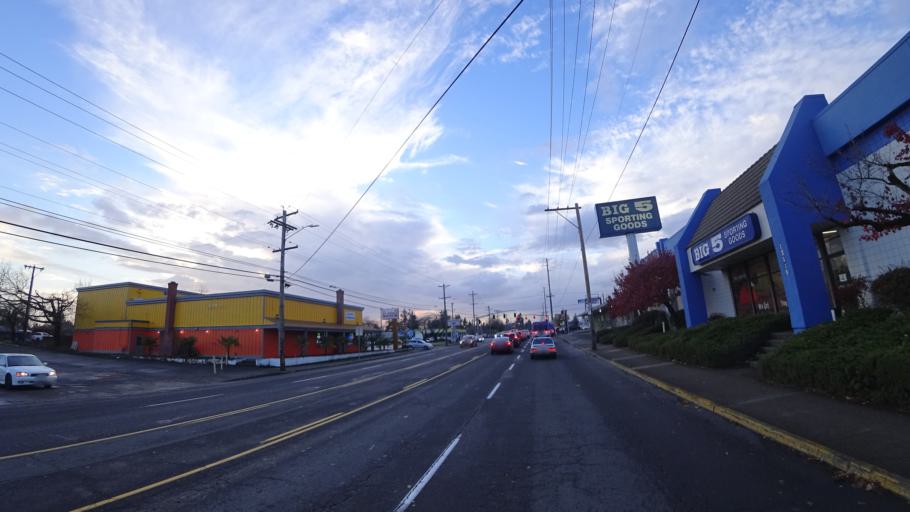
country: US
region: Oregon
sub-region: Multnomah County
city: Lents
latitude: 45.5191
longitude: -122.5363
